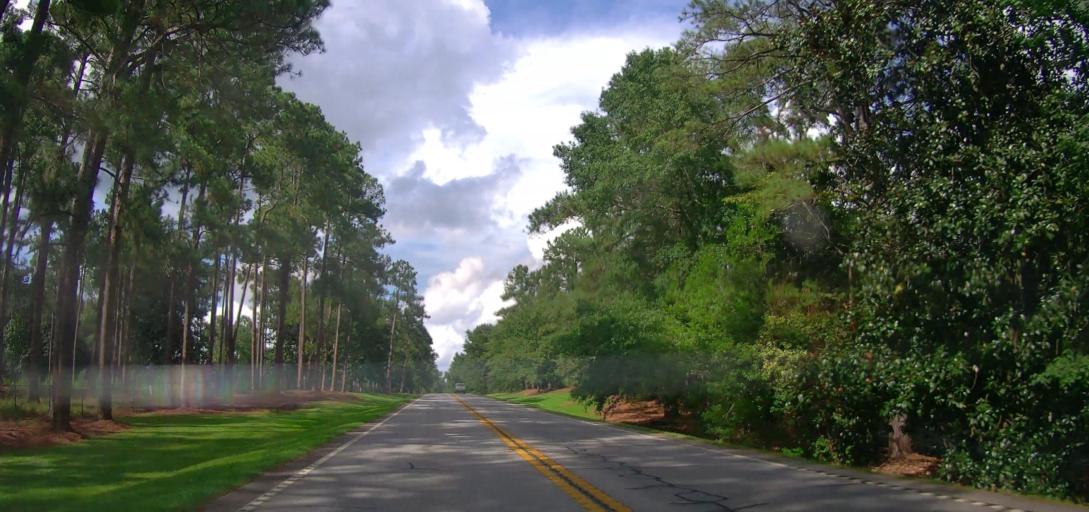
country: US
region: Georgia
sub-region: Harris County
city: Pine Mountain
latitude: 32.8347
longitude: -84.8437
